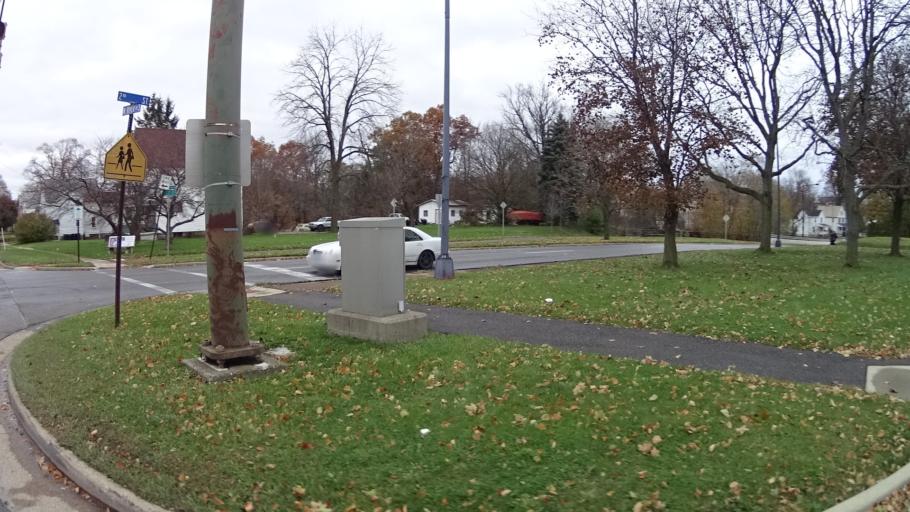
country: US
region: Ohio
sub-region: Lorain County
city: Elyria
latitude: 41.3660
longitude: -82.1161
